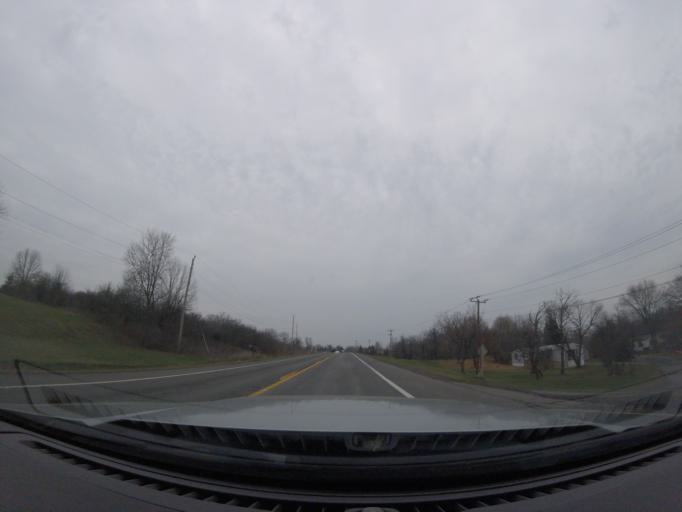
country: US
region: New York
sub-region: Yates County
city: Penn Yan
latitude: 42.6703
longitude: -76.9476
